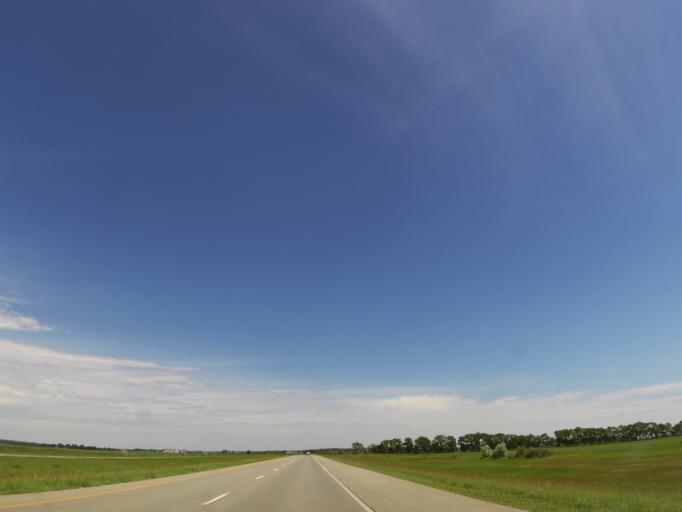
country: US
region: North Dakota
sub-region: Traill County
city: Hillsboro
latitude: 47.5596
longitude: -97.0802
